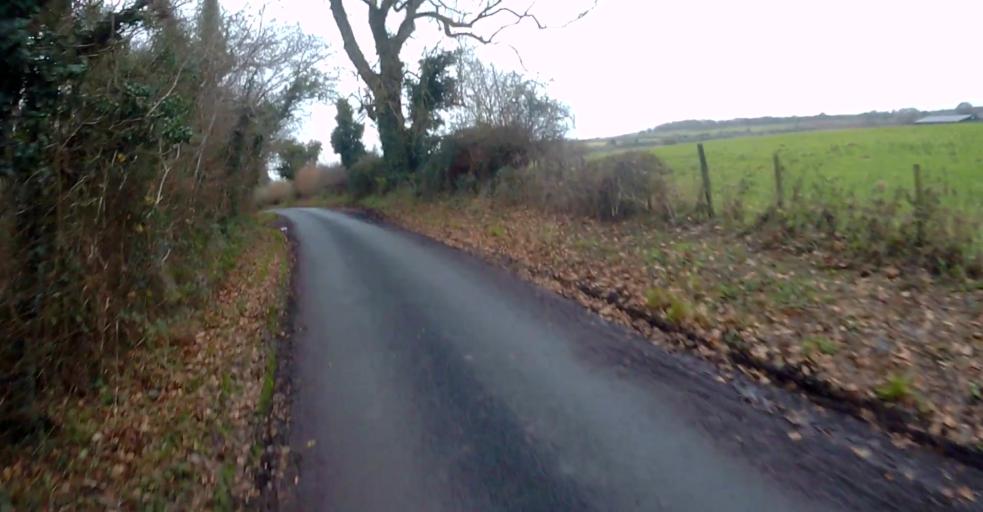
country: GB
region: England
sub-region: Hampshire
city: Overton
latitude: 51.2213
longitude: -1.2262
